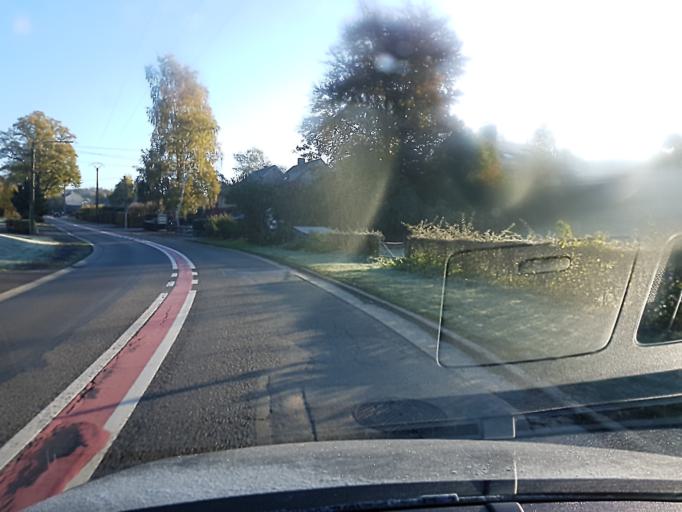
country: BE
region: Wallonia
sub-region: Province de Liege
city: Theux
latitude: 50.5391
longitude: 5.8238
